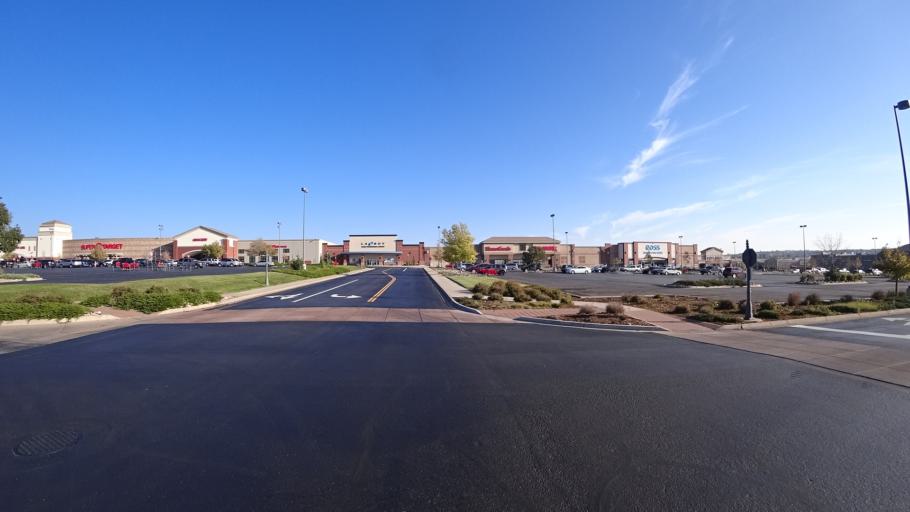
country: US
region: Colorado
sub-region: El Paso County
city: Cimarron Hills
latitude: 38.8871
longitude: -104.7169
